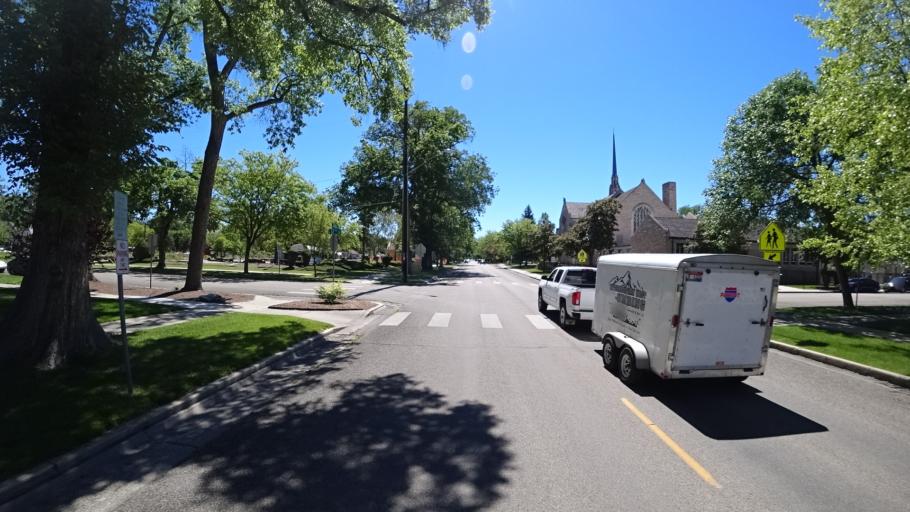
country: US
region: Idaho
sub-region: Ada County
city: Boise
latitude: 43.6235
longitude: -116.2032
